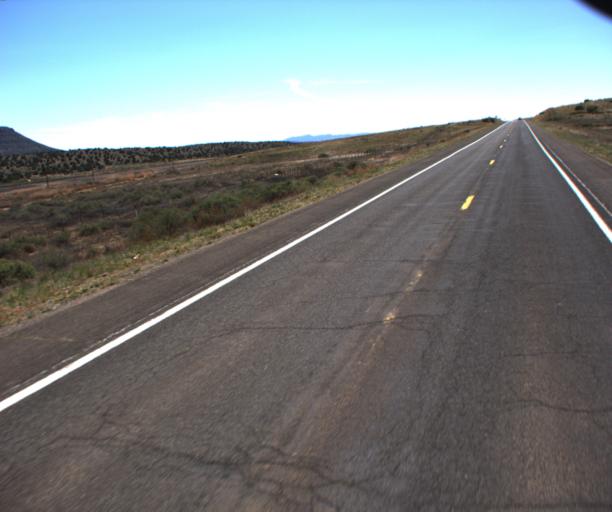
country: US
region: Arizona
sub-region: Mohave County
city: Peach Springs
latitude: 35.5239
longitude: -113.4440
